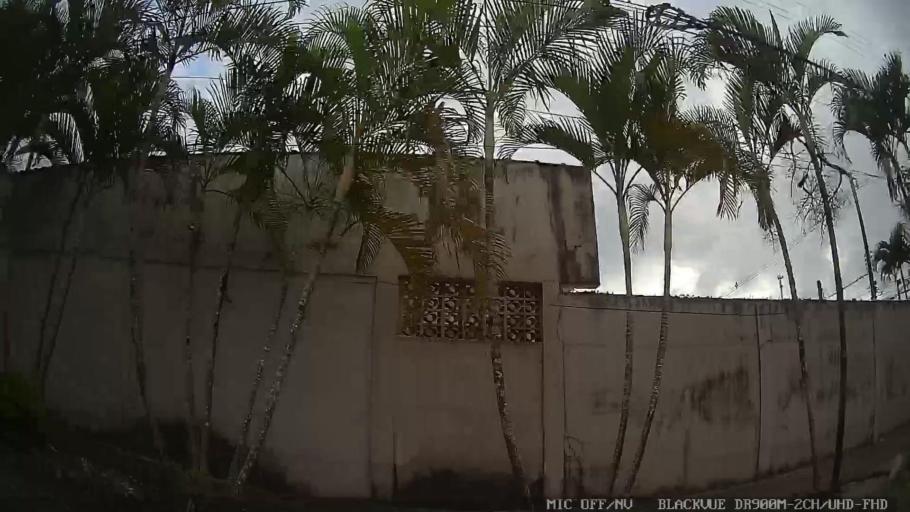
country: BR
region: Sao Paulo
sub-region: Itanhaem
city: Itanhaem
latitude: -24.1958
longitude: -46.8170
